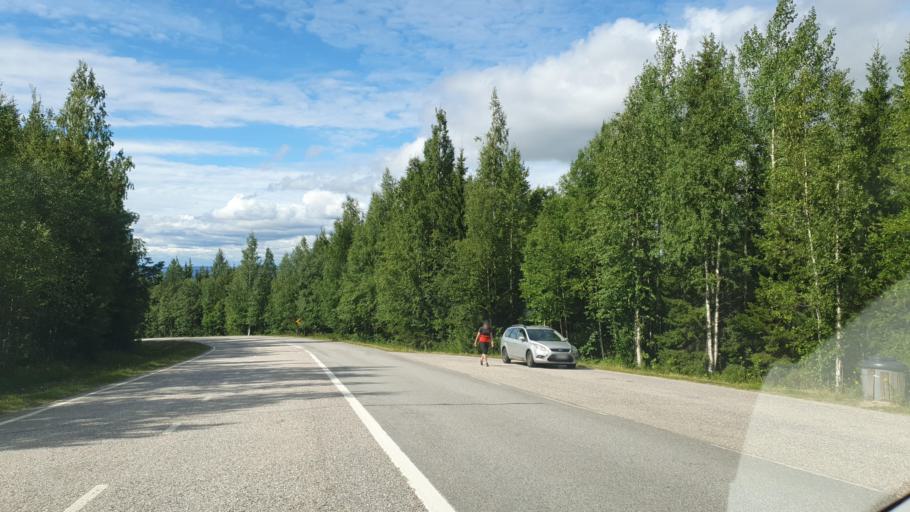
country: FI
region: Kainuu
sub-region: Kajaani
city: Vuokatti
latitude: 64.1303
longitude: 28.2520
